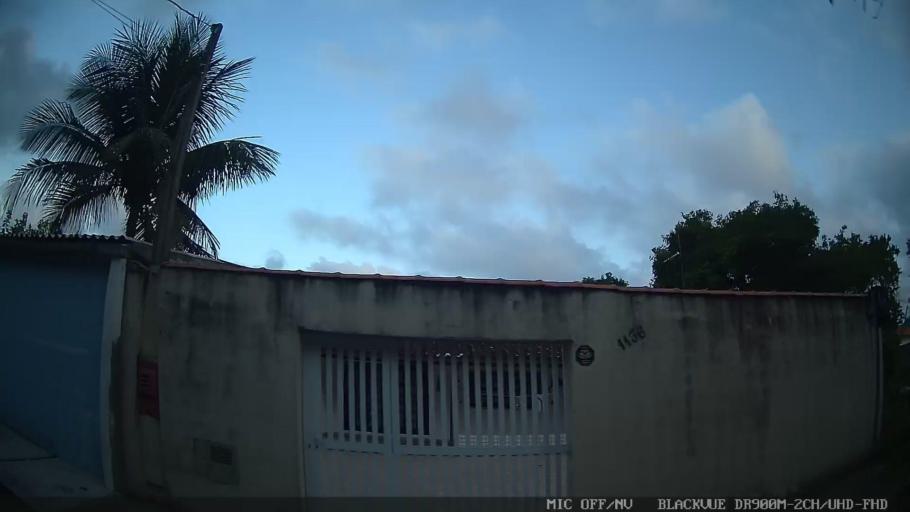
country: BR
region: Sao Paulo
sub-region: Peruibe
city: Peruibe
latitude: -24.3172
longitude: -47.0004
